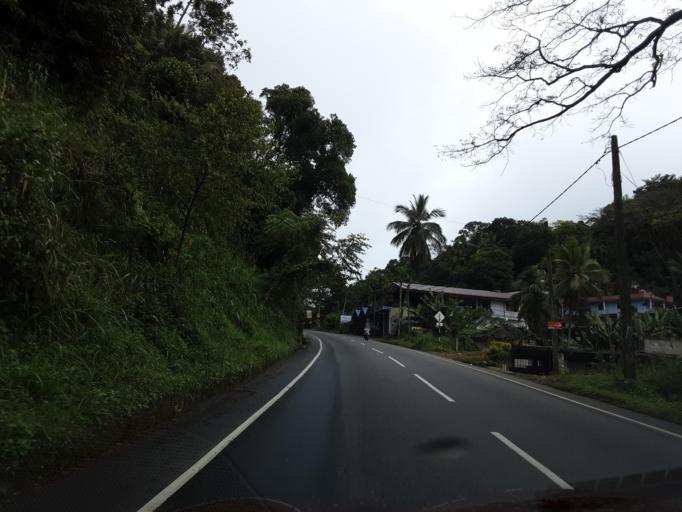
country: LK
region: Uva
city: Badulla
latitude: 7.0178
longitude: 81.0546
